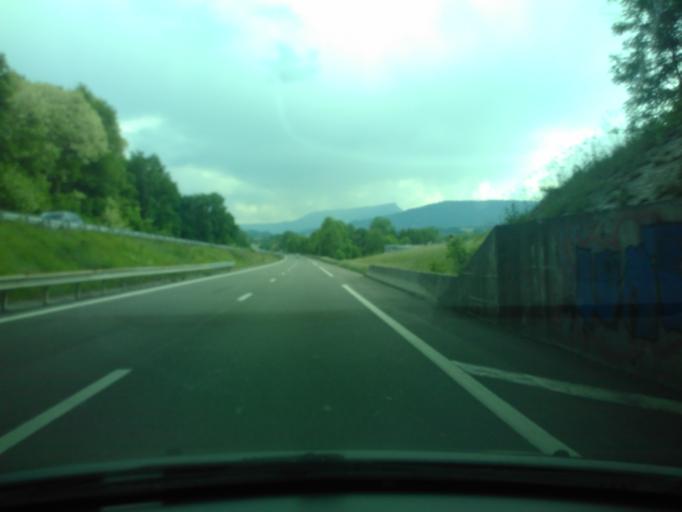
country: FR
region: Rhone-Alpes
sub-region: Departement de la Haute-Savoie
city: Saint-Felix
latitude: 45.7963
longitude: 5.9723
